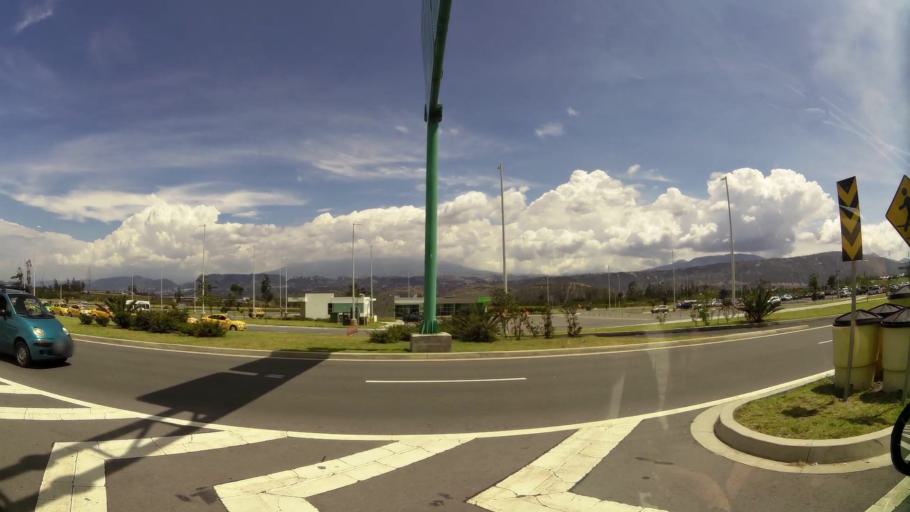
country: EC
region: Pichincha
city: Quito
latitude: -0.1269
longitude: -78.3608
